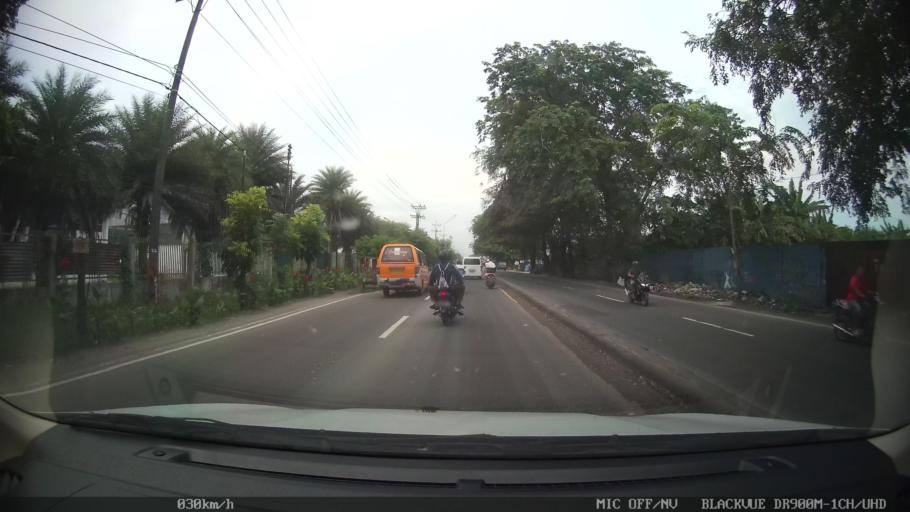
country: ID
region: North Sumatra
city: Sunggal
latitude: 3.5995
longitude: 98.5719
